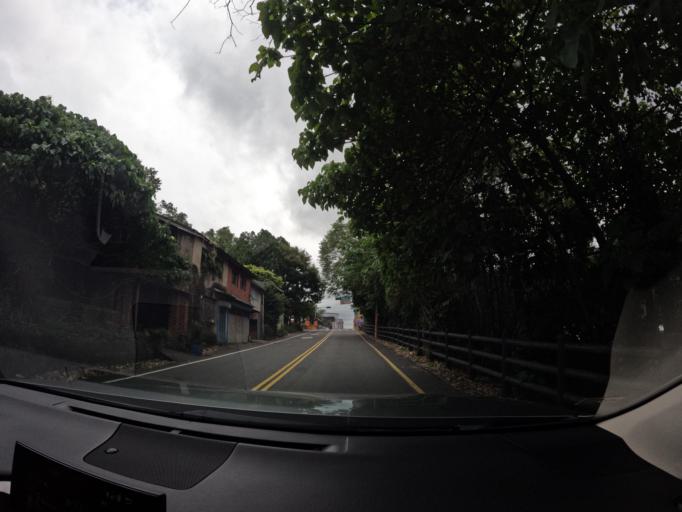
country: TW
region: Taiwan
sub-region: Miaoli
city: Miaoli
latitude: 24.4251
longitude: 120.8664
